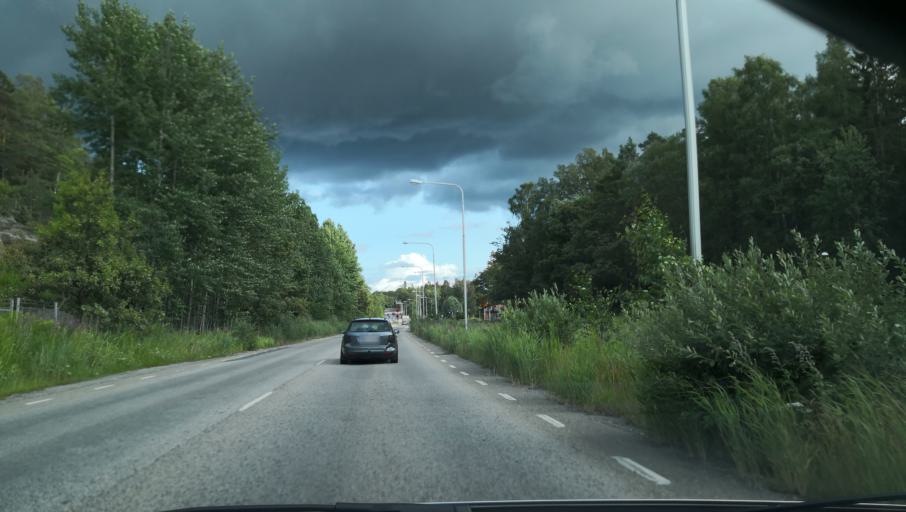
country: SE
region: Stockholm
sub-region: Stockholms Kommun
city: Arsta
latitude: 59.2500
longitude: 18.0623
